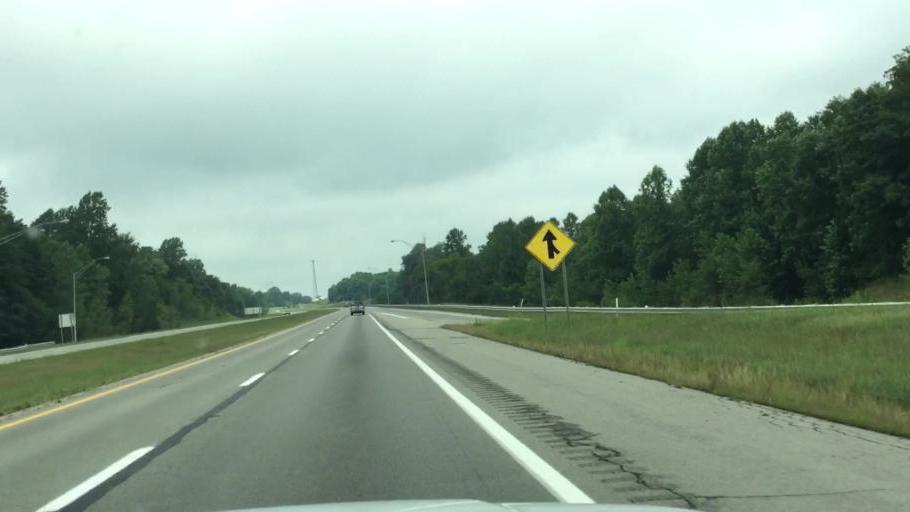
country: US
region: Ohio
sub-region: Logan County
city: Bellefontaine
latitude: 40.3435
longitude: -83.6951
